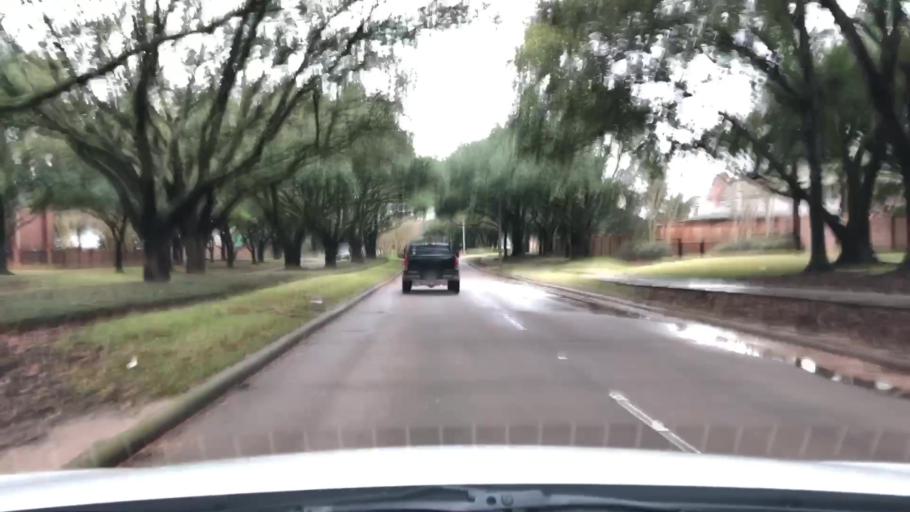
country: US
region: Texas
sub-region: Fort Bend County
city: Cinco Ranch
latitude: 29.7409
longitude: -95.7542
